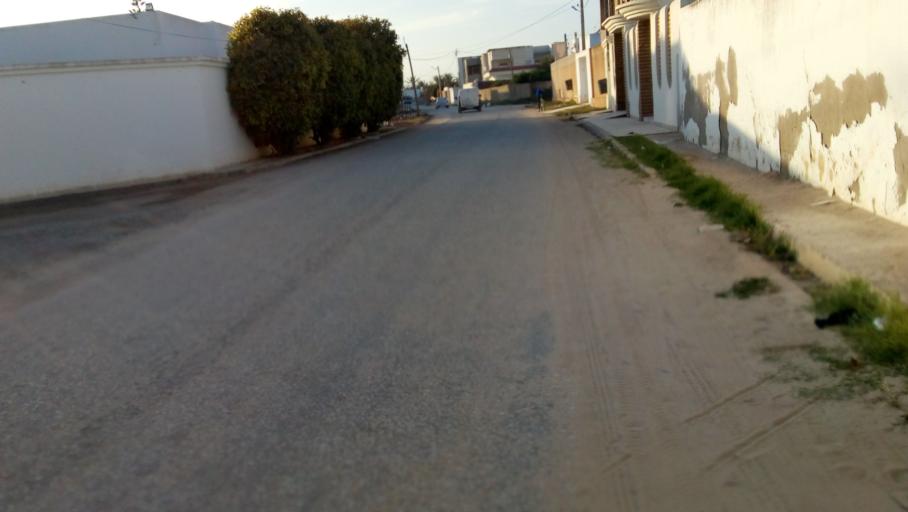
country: TN
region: Safaqis
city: Sfax
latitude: 34.7526
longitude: 10.7341
